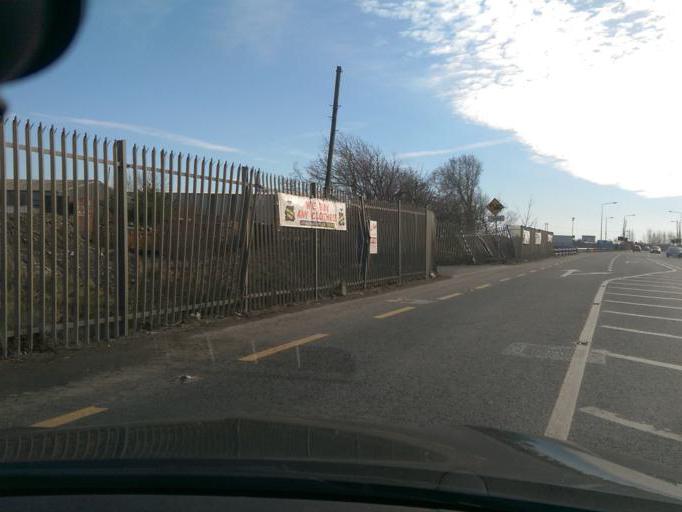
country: IE
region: Connaught
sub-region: County Galway
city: Oranmore
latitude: 53.2815
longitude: -8.9259
